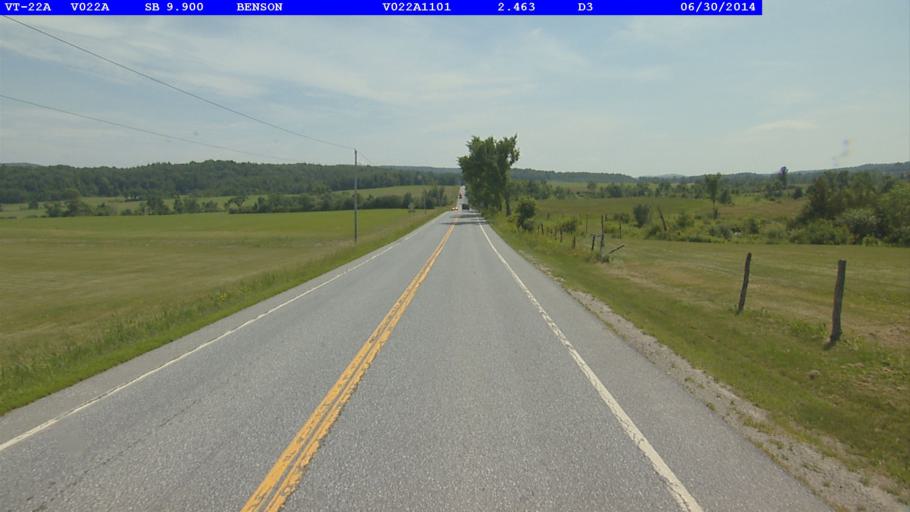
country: US
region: Vermont
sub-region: Rutland County
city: Fair Haven
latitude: 43.7039
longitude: -73.2959
